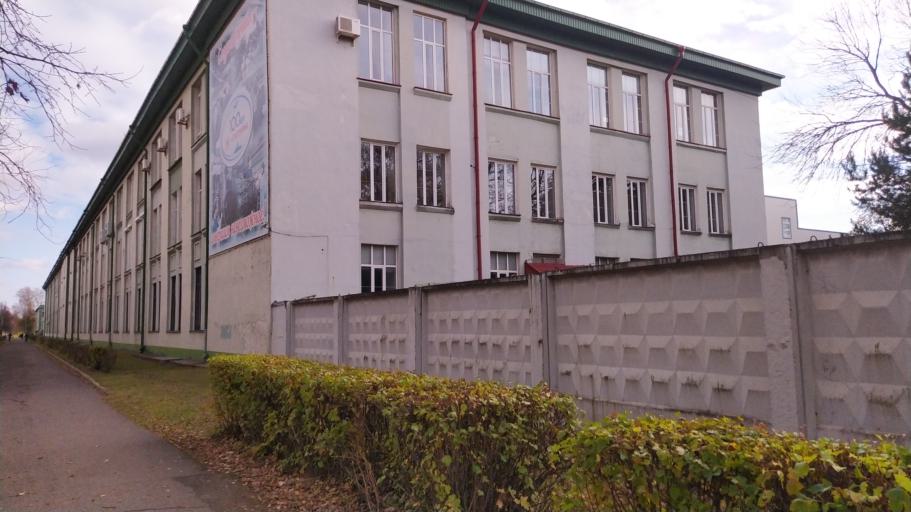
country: RU
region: Jaroslavl
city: Rybinsk
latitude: 58.0565
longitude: 38.7935
